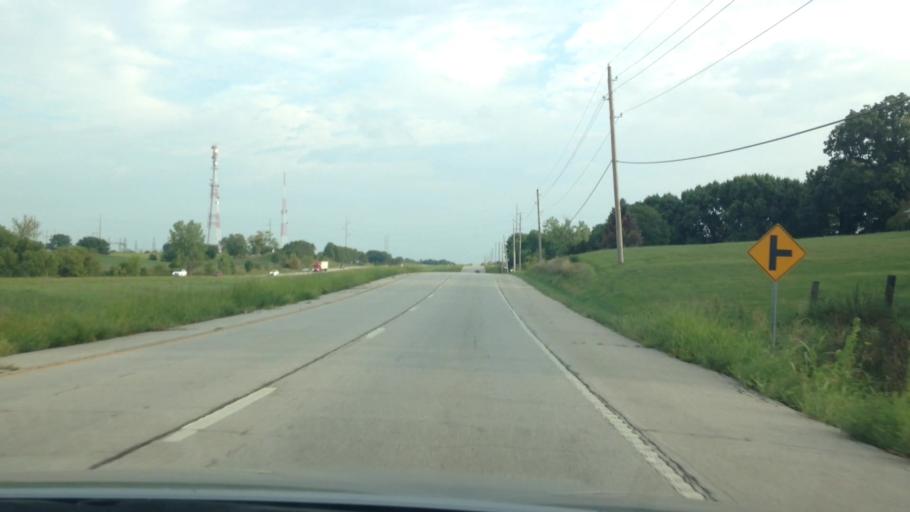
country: US
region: Missouri
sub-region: Clay County
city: Smithville
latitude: 39.3386
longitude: -94.5844
